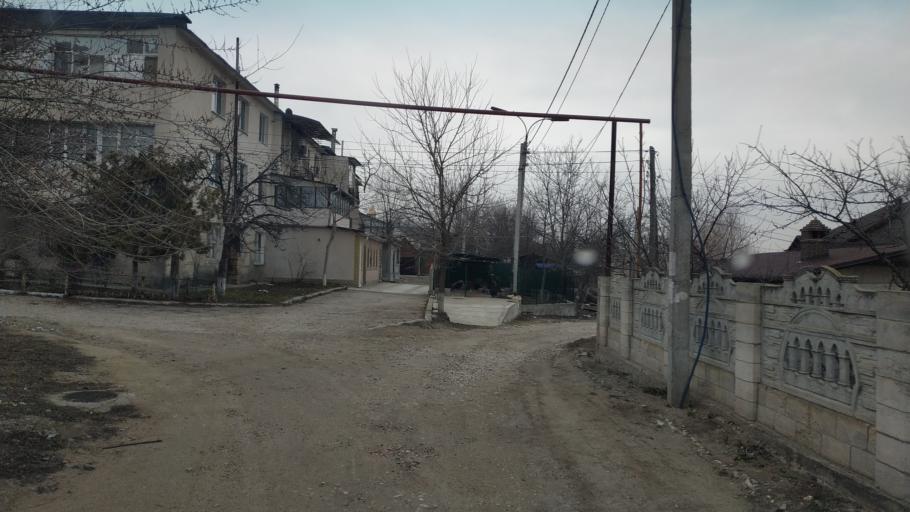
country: MD
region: Chisinau
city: Singera
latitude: 46.9229
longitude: 28.9659
